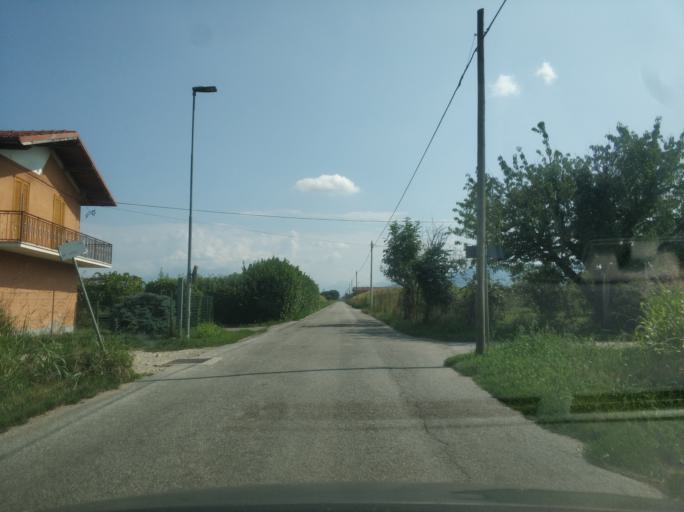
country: IT
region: Piedmont
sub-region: Provincia di Cuneo
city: Caraglio
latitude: 44.4324
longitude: 7.4328
